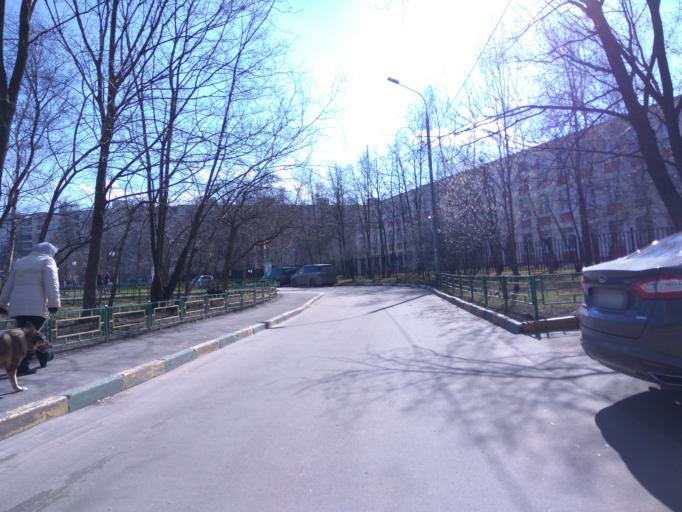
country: RU
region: Moscow
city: Ivanovskoye
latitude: 55.7737
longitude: 37.8366
